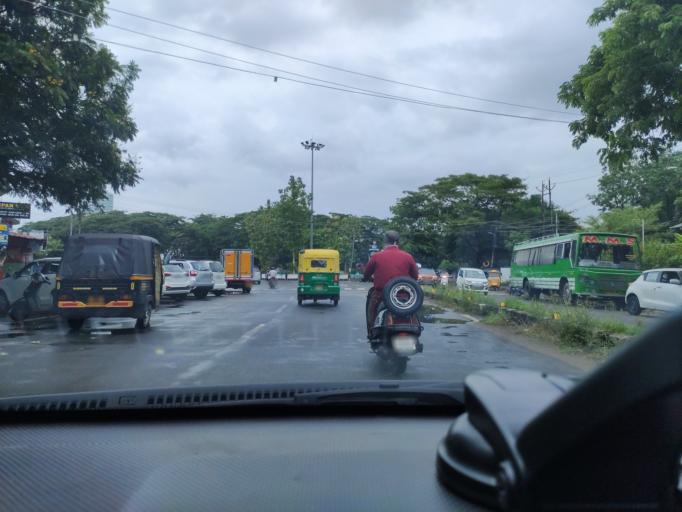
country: IN
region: Kerala
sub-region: Ernakulam
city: Elur
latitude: 10.0215
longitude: 76.3340
